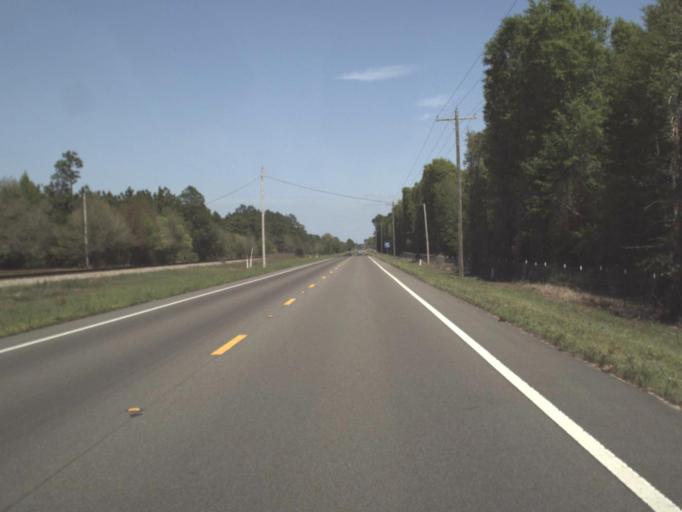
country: US
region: Florida
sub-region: Okaloosa County
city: Crestview
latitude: 30.6997
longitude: -86.7903
